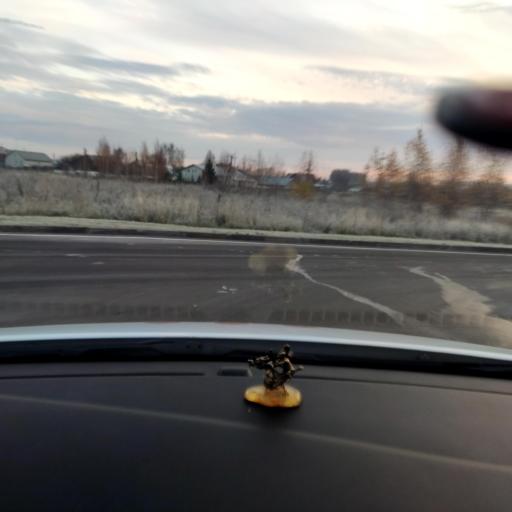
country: RU
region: Tatarstan
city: Osinovo
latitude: 55.8622
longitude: 48.8350
